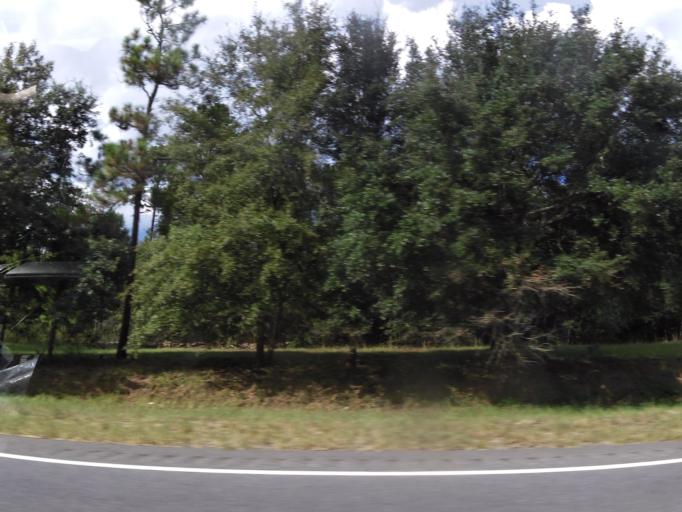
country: US
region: Georgia
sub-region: Lowndes County
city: Remerton
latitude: 30.8002
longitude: -83.3824
